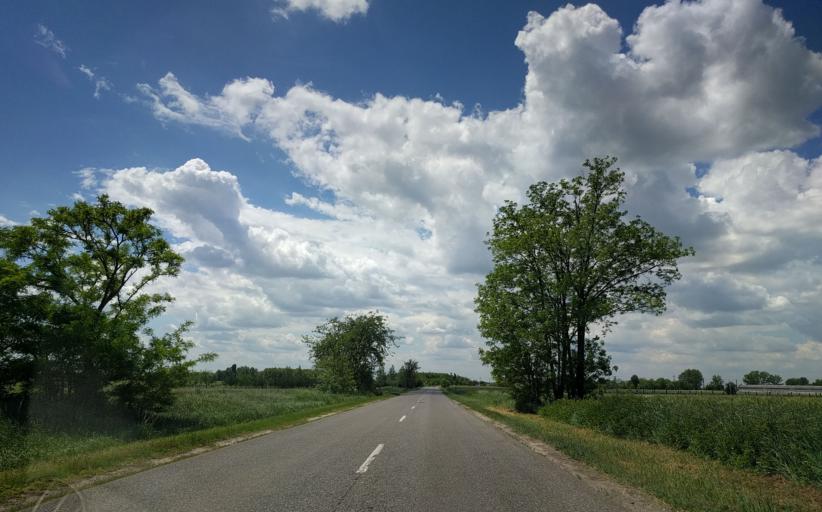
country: HU
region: Pest
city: Jaszkarajeno
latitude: 47.0155
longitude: 20.1318
